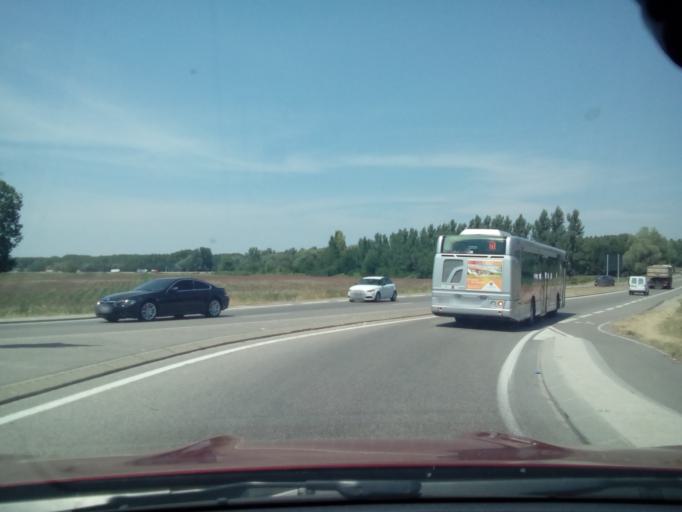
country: FR
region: Rhone-Alpes
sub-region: Departement de l'Isere
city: Domarin
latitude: 45.6003
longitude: 5.2501
